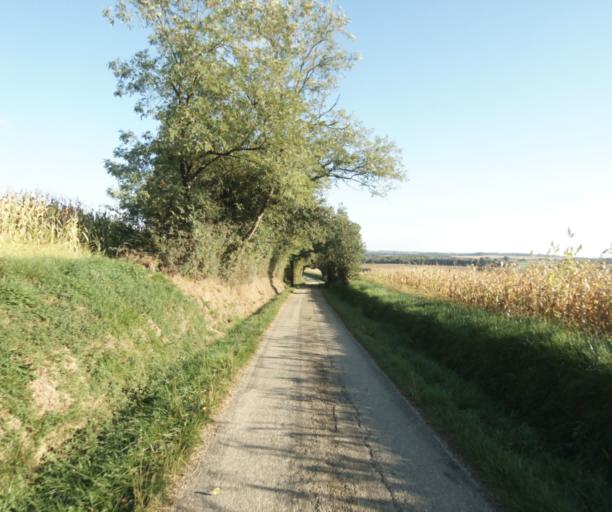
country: FR
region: Midi-Pyrenees
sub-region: Departement du Gers
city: Eauze
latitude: 43.7670
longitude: 0.1385
